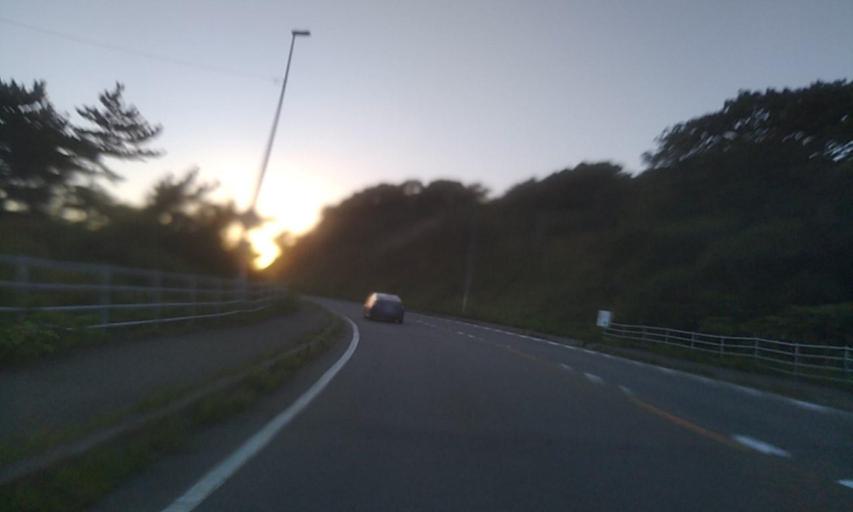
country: JP
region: Hokkaido
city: Shizunai-furukawacho
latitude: 42.1585
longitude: 142.7866
